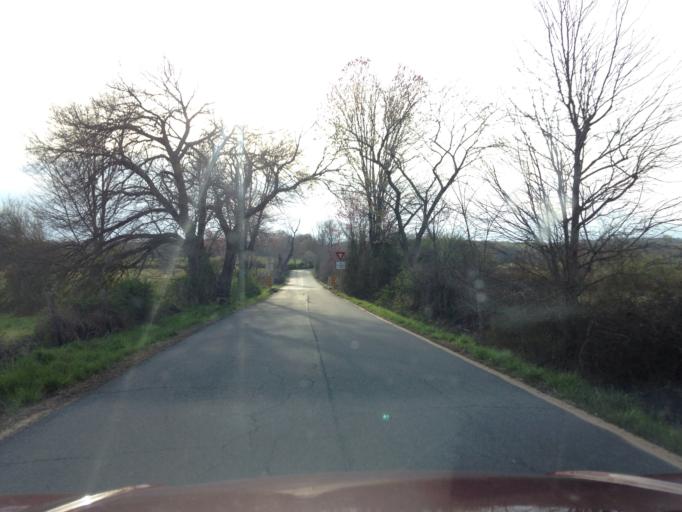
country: US
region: Maryland
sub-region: Frederick County
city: Point of Rocks
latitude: 39.2043
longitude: -77.5392
